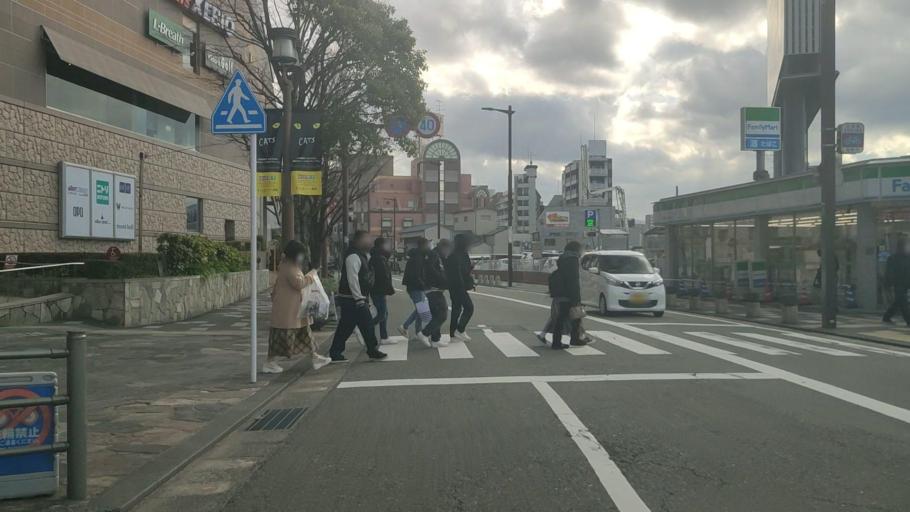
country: JP
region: Fukuoka
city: Fukuoka-shi
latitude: 33.5892
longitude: 130.4102
